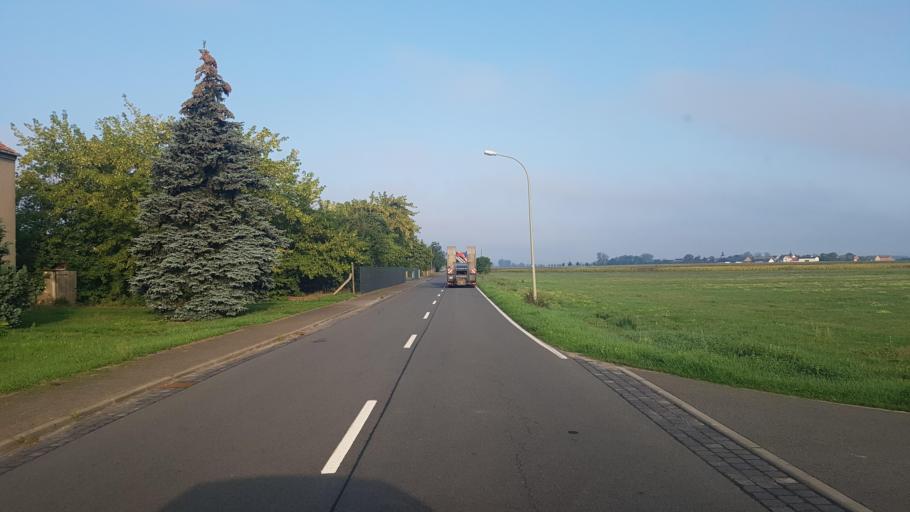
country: DE
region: Saxony-Anhalt
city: Prettin
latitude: 51.7019
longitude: 12.8832
